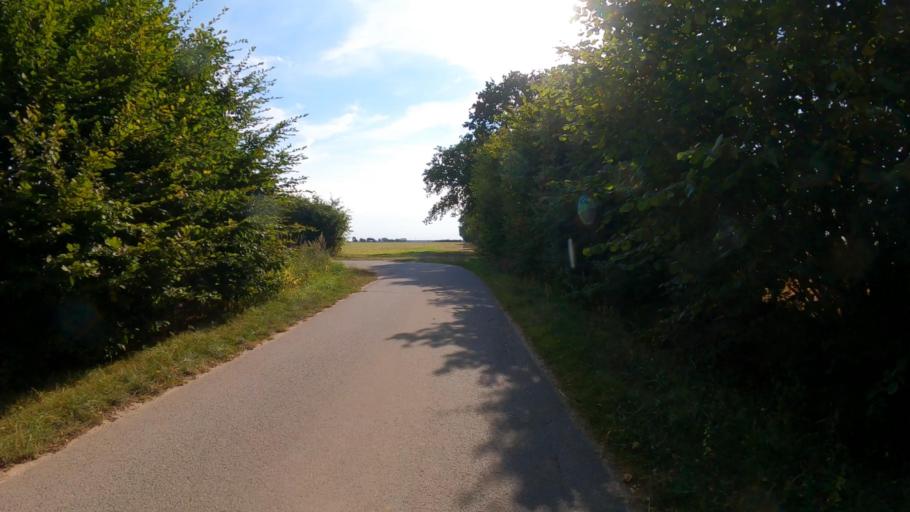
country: DE
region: Schleswig-Holstein
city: Dassendorf
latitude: 53.4955
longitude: 10.3843
